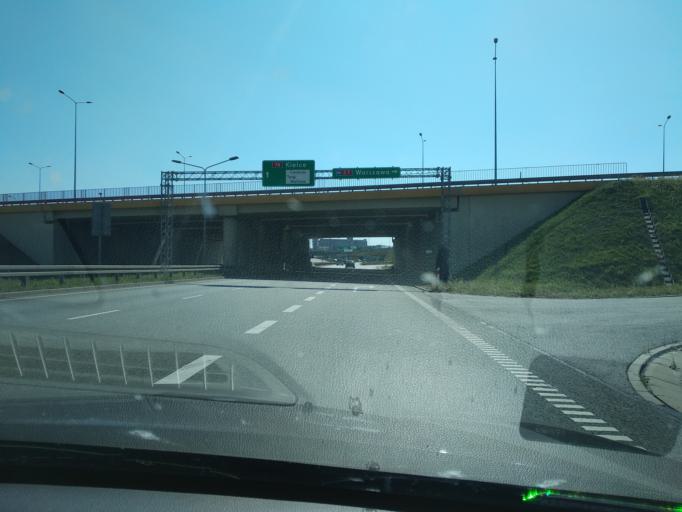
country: PL
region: Swietokrzyskie
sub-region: Powiat kielecki
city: Kostomloty Pierwsze
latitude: 50.9091
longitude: 20.5789
